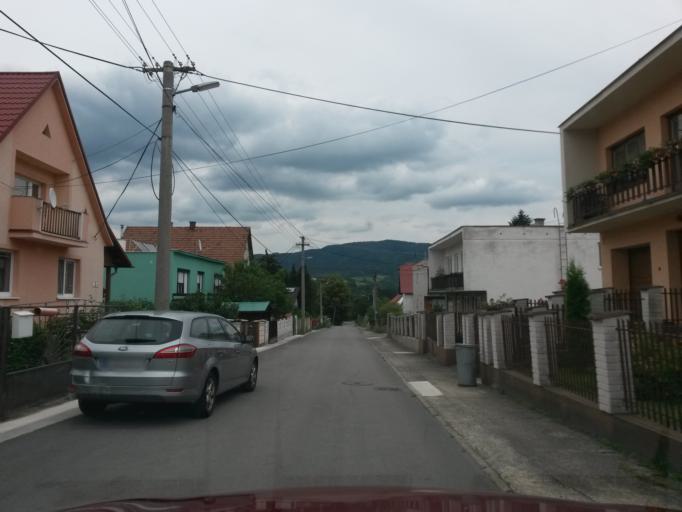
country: SK
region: Nitriansky
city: Handlova
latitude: 48.7343
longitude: 18.7493
